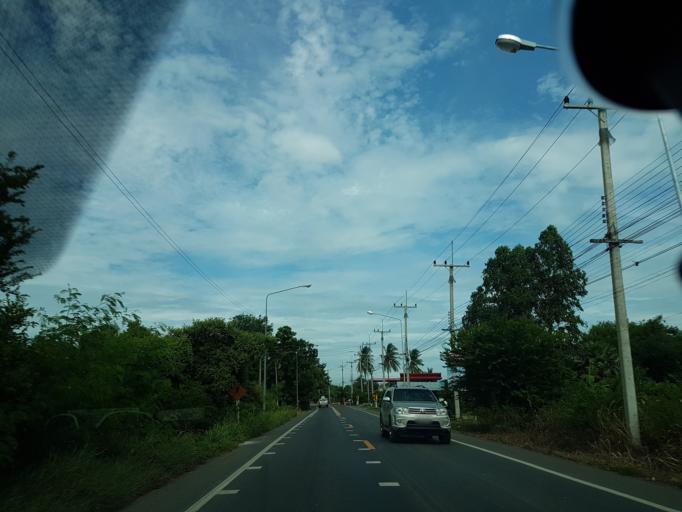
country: TH
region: Lop Buri
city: Tha Wung
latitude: 14.7404
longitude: 100.5326
